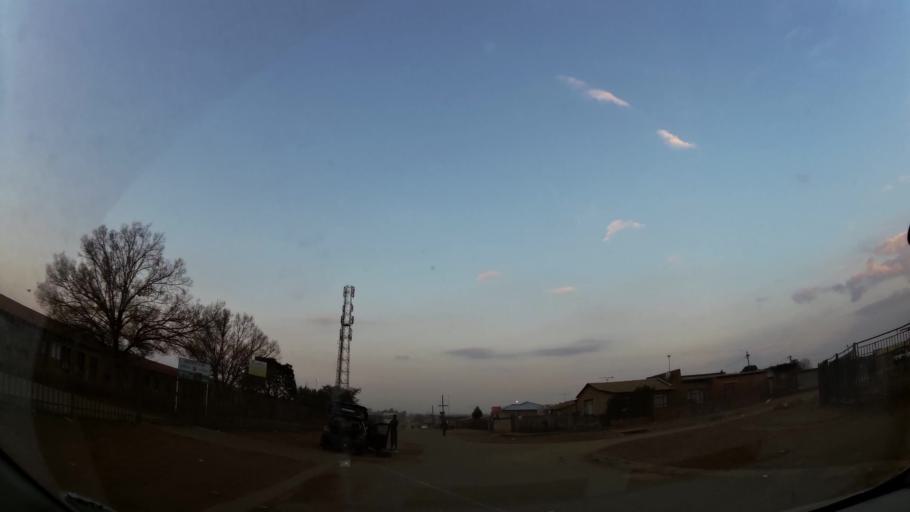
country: ZA
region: Gauteng
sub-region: City of Johannesburg Metropolitan Municipality
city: Orange Farm
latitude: -26.5536
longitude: 27.8686
